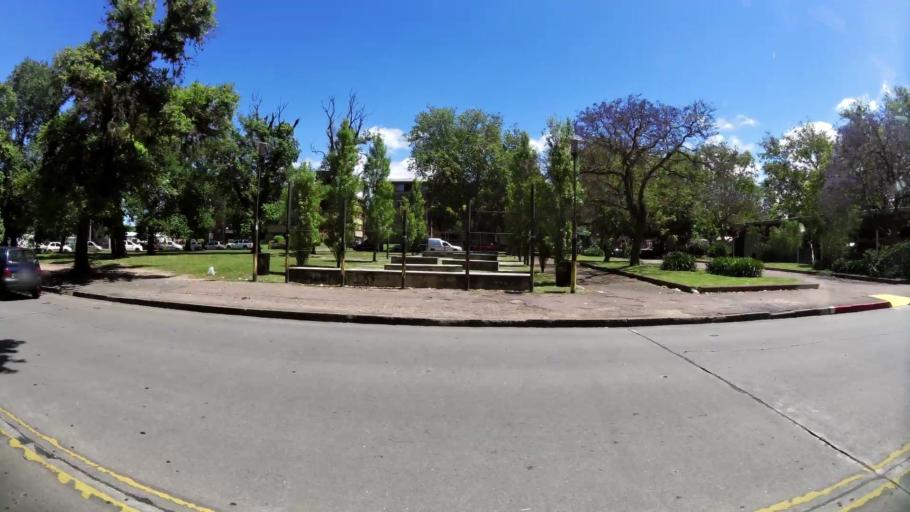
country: UY
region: Montevideo
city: Montevideo
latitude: -34.8993
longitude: -56.1281
